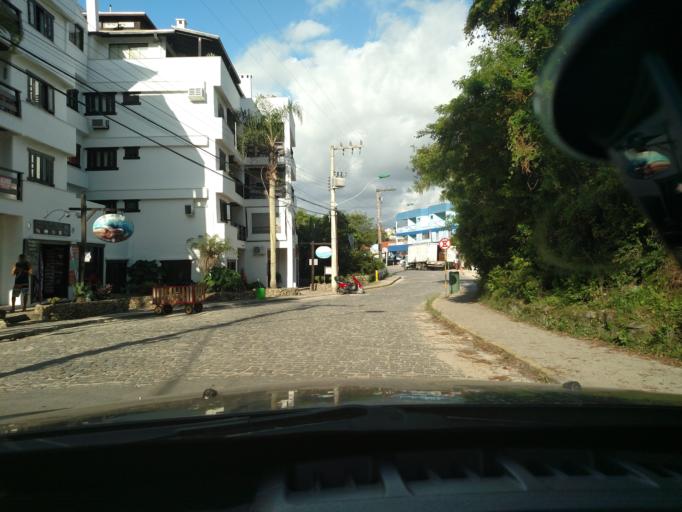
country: BR
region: Santa Catarina
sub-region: Porto Belo
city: Porto Belo
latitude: -27.1485
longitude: -48.4825
